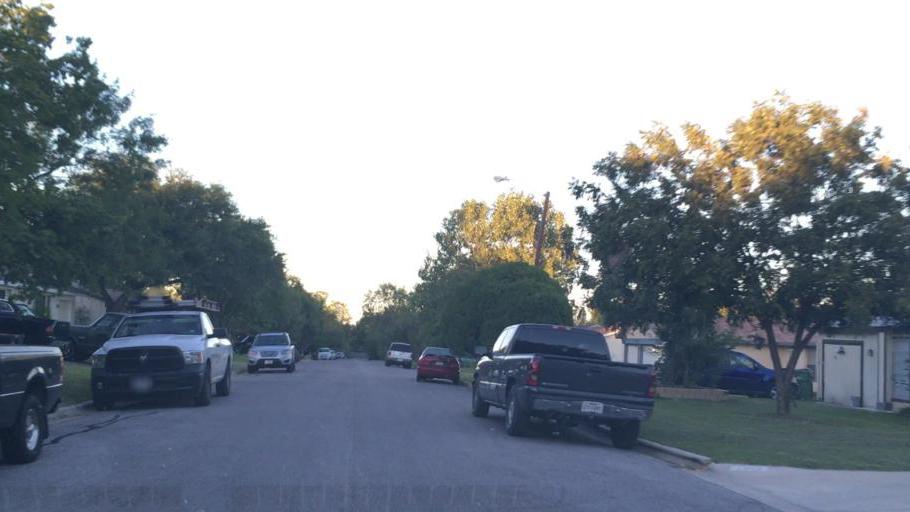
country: US
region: Texas
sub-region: Williamson County
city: Round Rock
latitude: 30.4985
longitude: -97.6634
